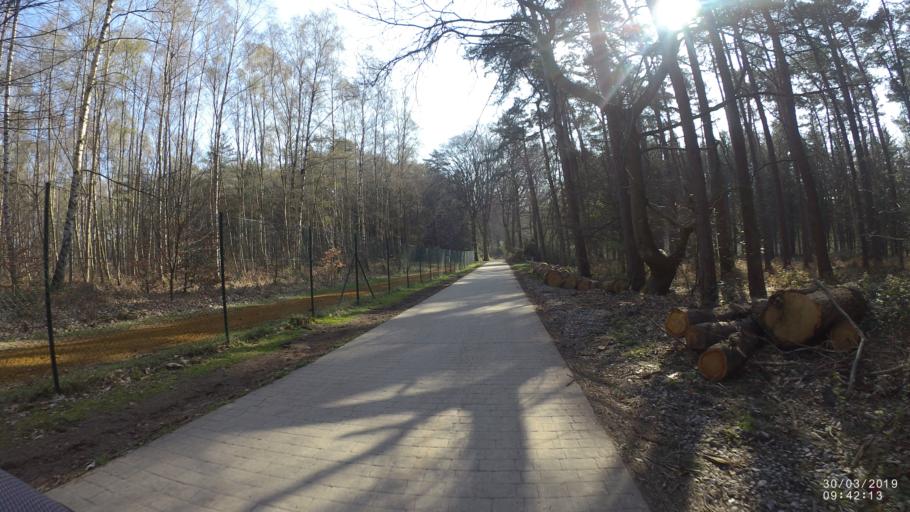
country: BE
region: Wallonia
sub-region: Province du Brabant Wallon
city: Louvain-la-Neuve
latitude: 50.6819
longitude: 4.5946
